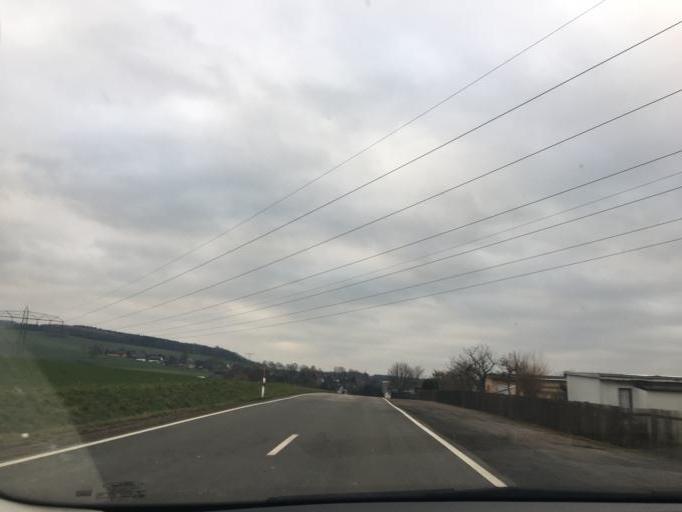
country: DE
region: Saxony
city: Hohenstein-Ernstthal
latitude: 50.8366
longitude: 12.7123
